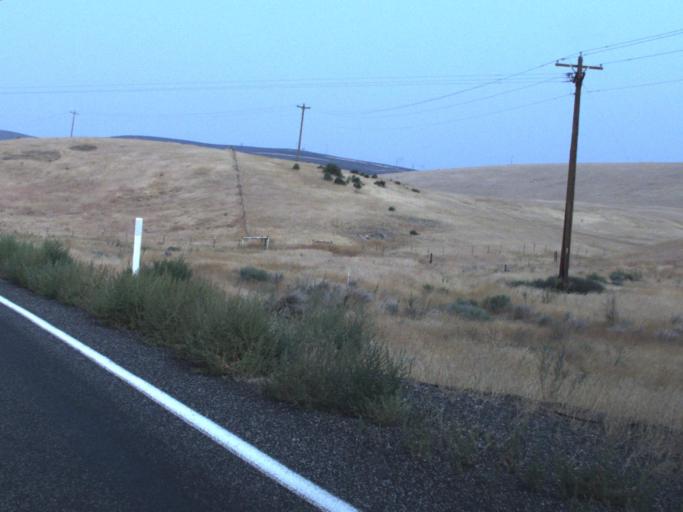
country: US
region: Washington
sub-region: Grant County
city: Desert Aire
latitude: 46.5264
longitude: -119.8743
